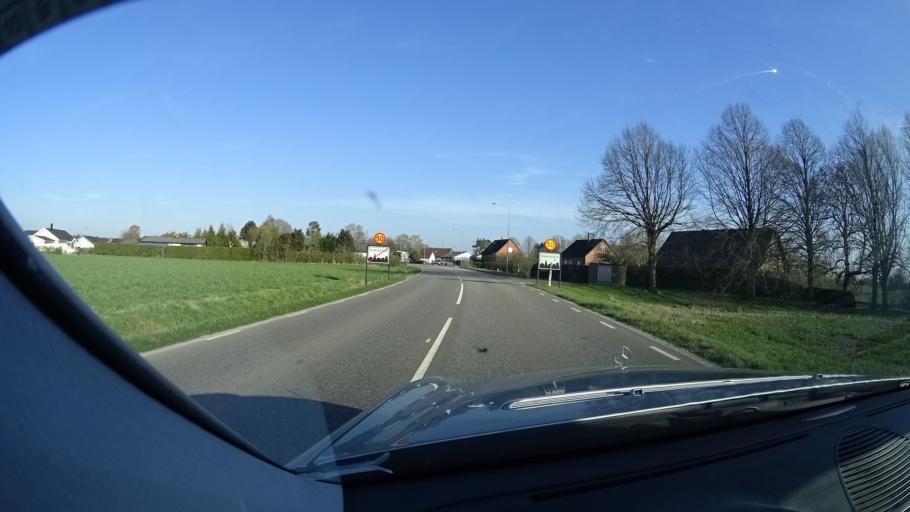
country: SE
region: Skane
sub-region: Svalovs Kommun
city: Teckomatorp
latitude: 55.8640
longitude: 13.1426
